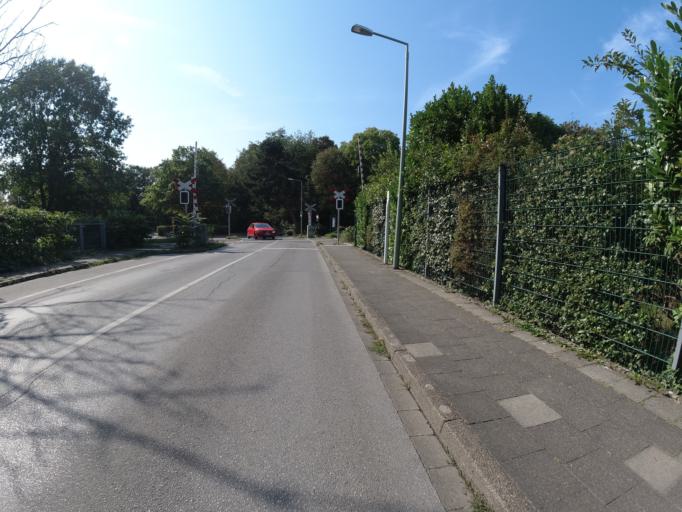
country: DE
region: North Rhine-Westphalia
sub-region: Regierungsbezirk Dusseldorf
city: Moers
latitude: 51.4589
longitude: 6.6874
